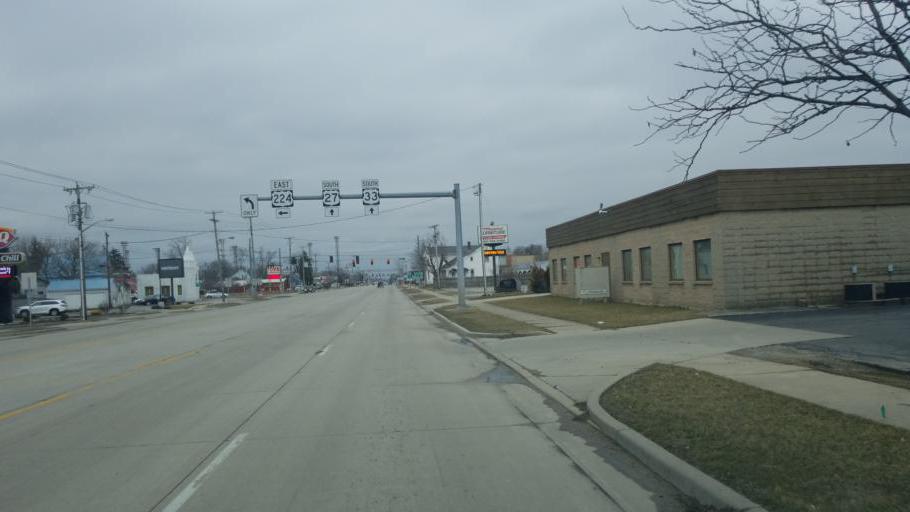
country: US
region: Indiana
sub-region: Adams County
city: Decatur
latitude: 40.8307
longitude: -84.9378
